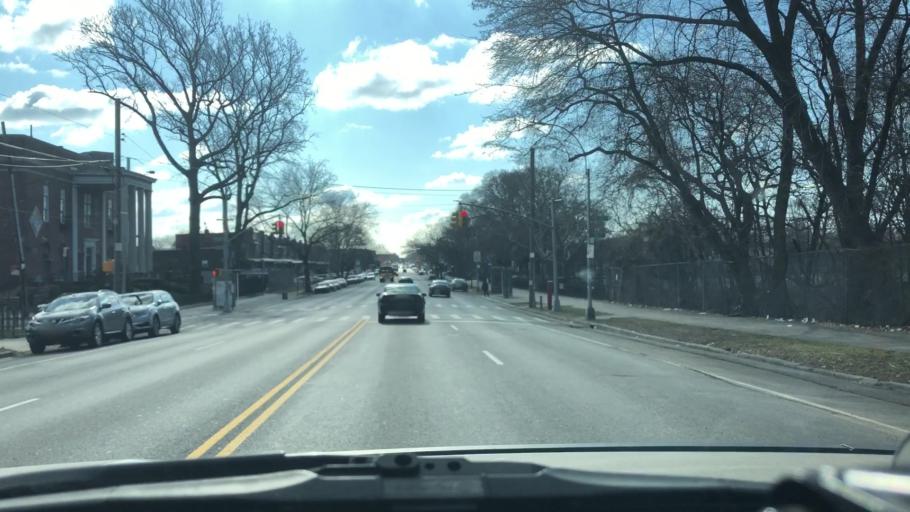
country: US
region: New York
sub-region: Kings County
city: Bensonhurst
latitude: 40.6143
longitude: -74.0144
